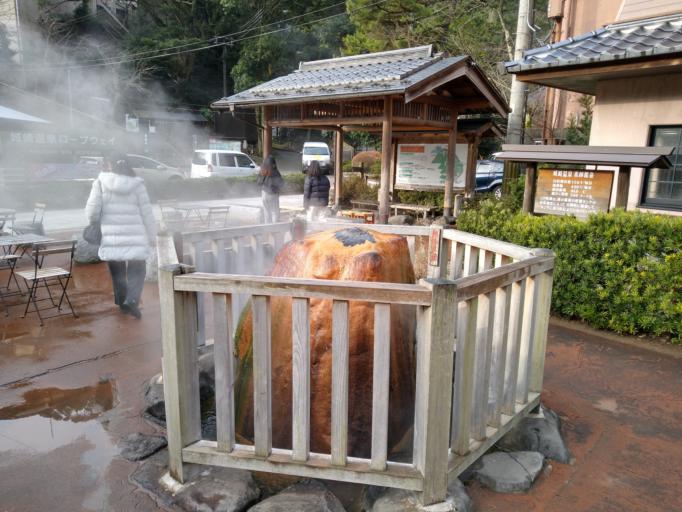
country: JP
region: Hyogo
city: Toyooka
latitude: 35.6257
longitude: 134.8043
